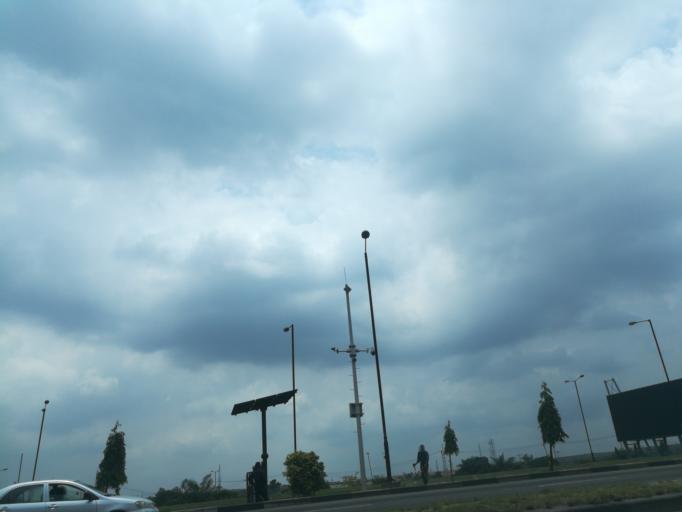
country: NG
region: Lagos
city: Ojota
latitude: 6.5947
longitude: 3.3824
